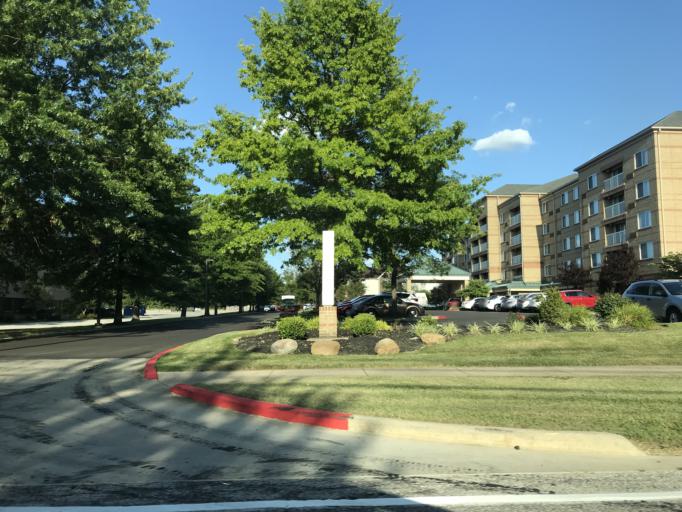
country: US
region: Ohio
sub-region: Cuyahoga County
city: Middleburg Heights
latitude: 41.3678
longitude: -81.8249
